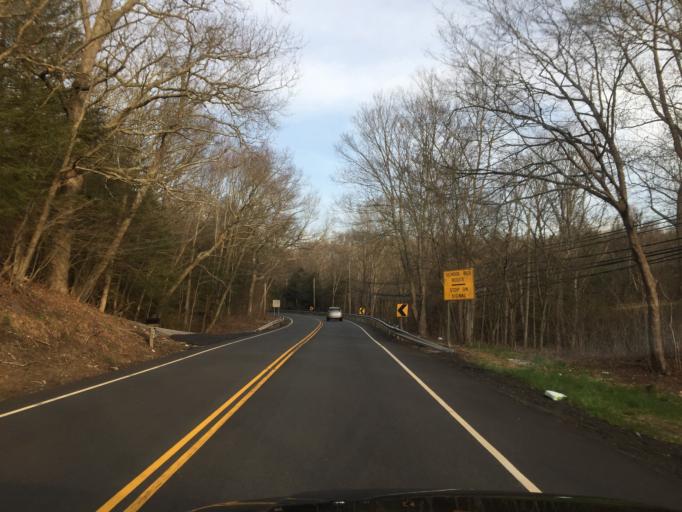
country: US
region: Connecticut
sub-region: Middlesex County
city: Moodus
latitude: 41.5503
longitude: -72.4461
